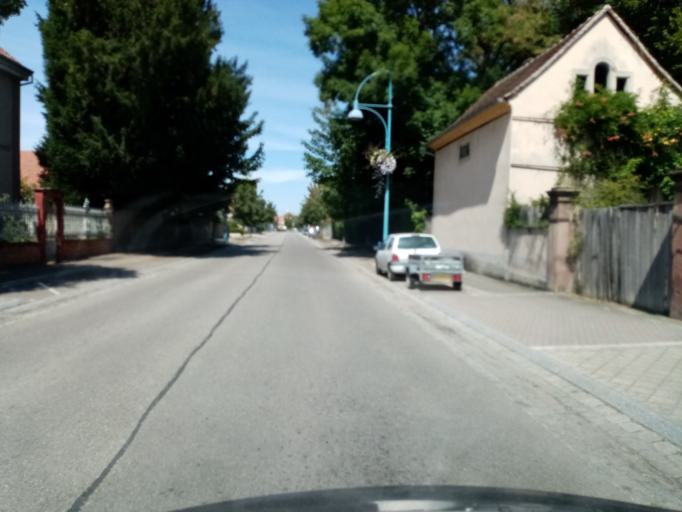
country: FR
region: Alsace
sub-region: Departement du Bas-Rhin
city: Marckolsheim
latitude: 48.1681
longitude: 7.5464
